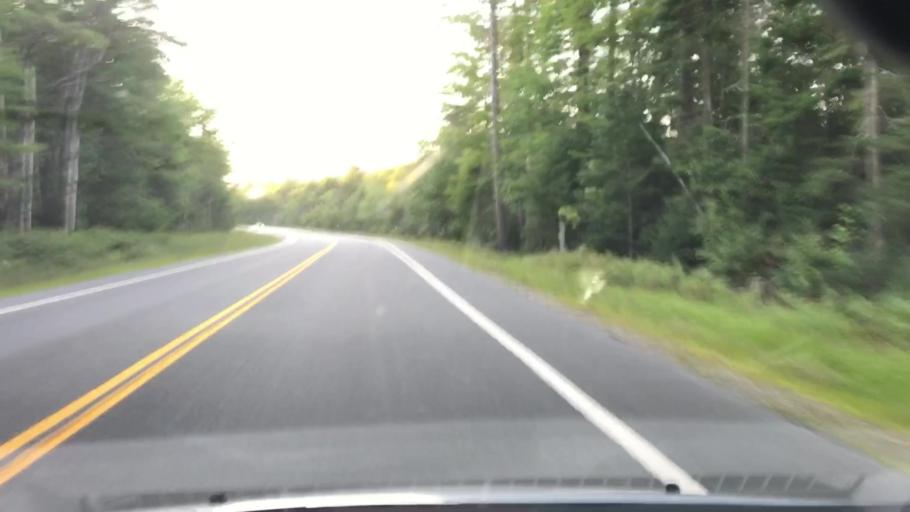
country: US
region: New Hampshire
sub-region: Grafton County
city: Rumney
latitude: 43.9612
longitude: -71.8860
